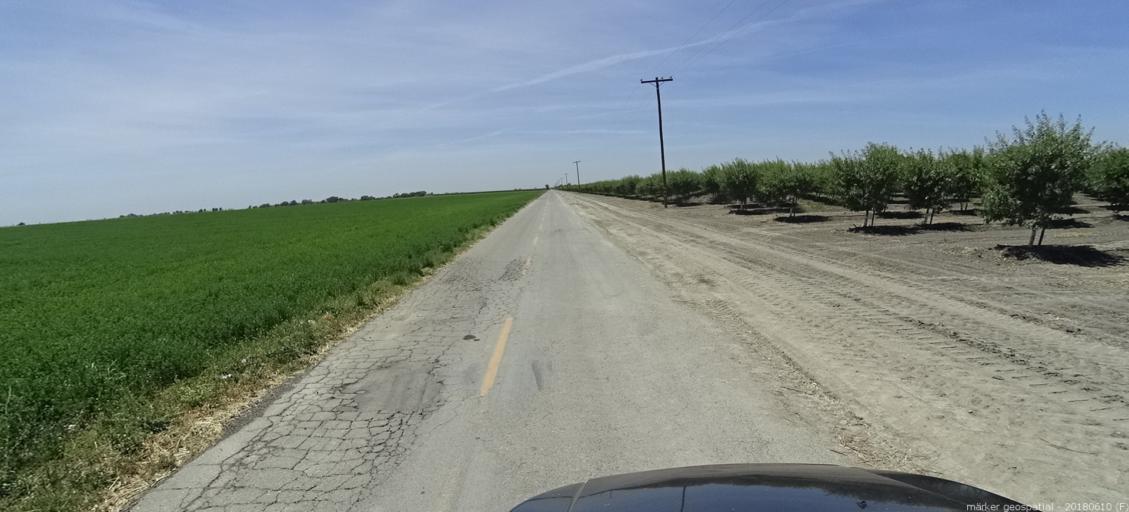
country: US
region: California
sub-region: Merced County
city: Dos Palos
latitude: 37.0383
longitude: -120.5287
